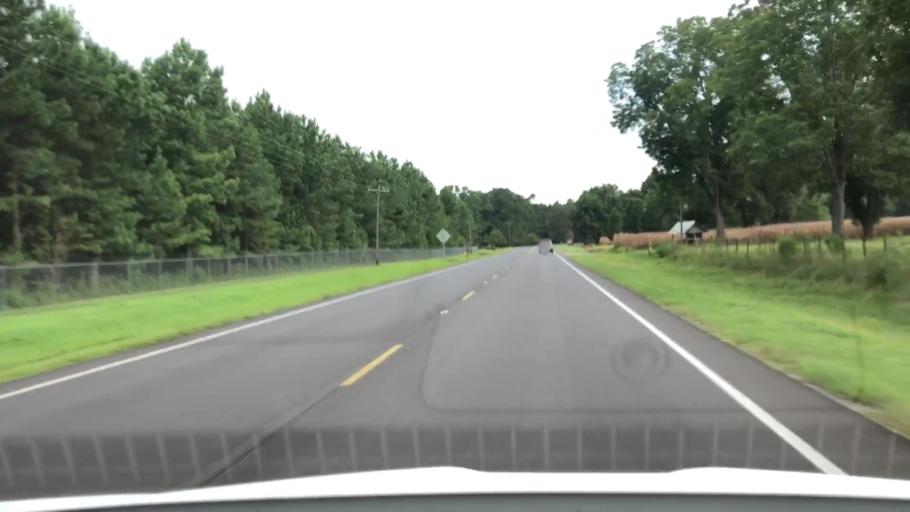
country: US
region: North Carolina
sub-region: Jones County
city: Maysville
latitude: 34.8850
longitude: -77.2110
